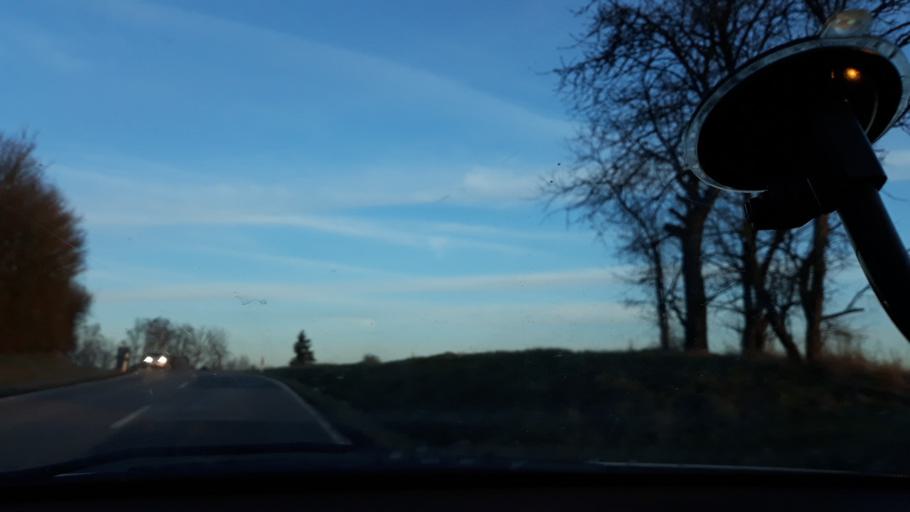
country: DE
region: Saarland
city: Sankt Ingbert
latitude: 49.2208
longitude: 7.1488
